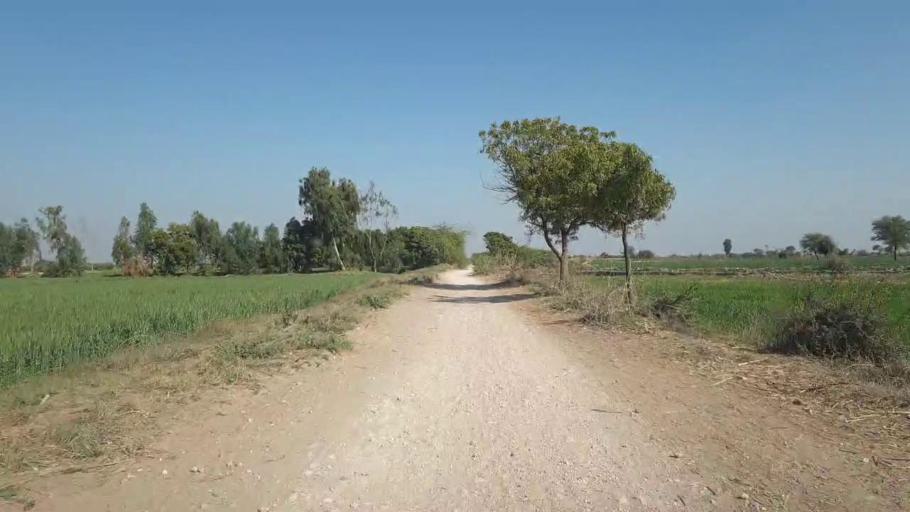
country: PK
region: Sindh
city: Pithoro
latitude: 25.3987
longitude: 69.2641
